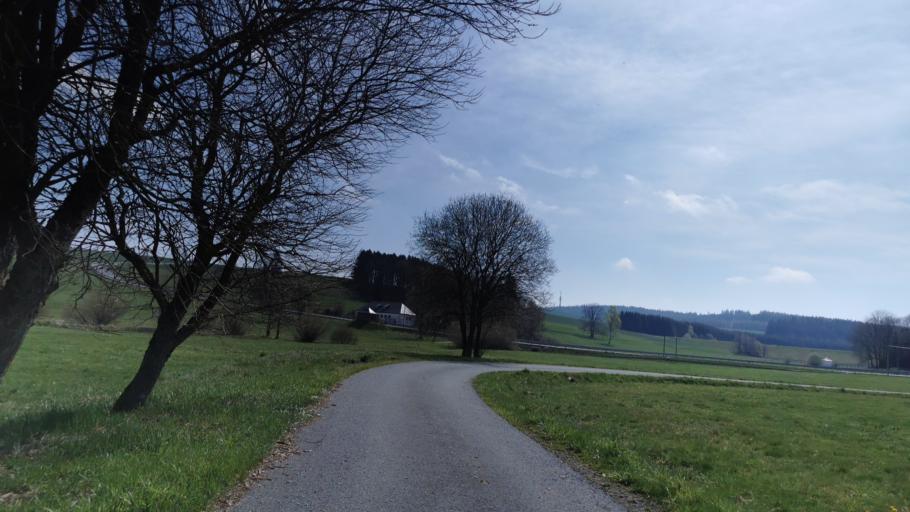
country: DE
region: Thuringia
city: Schlegel
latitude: 50.4321
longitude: 11.5791
